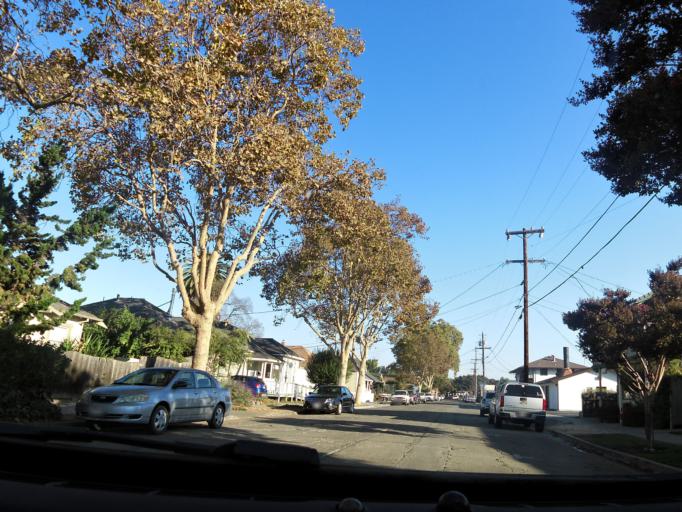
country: US
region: California
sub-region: San Benito County
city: Hollister
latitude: 36.8465
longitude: -121.4031
